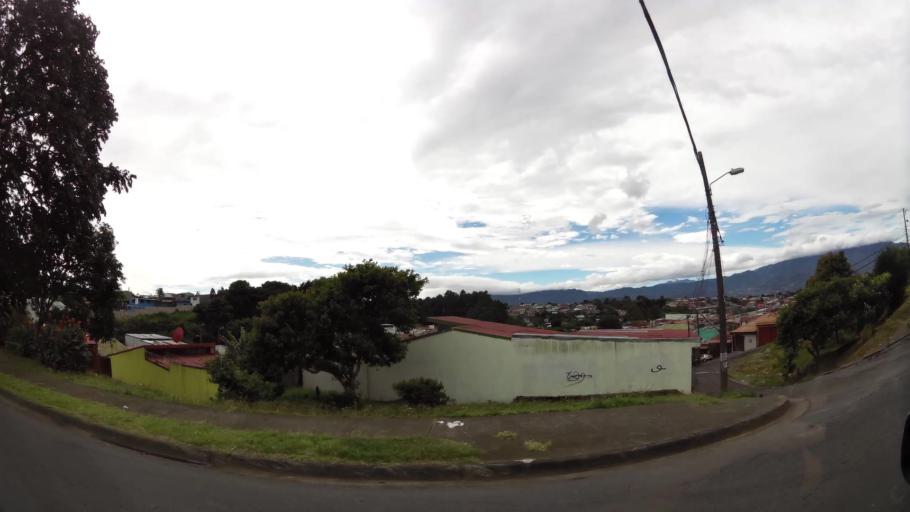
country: CR
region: San Jose
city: Purral
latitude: 9.9589
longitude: -84.0223
